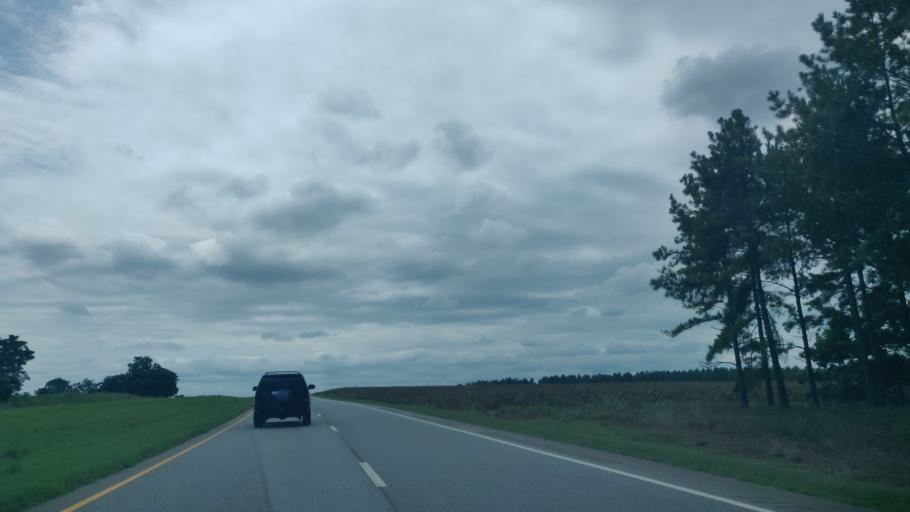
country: US
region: Georgia
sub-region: Terrell County
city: Dawson
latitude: 31.8594
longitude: -84.4821
